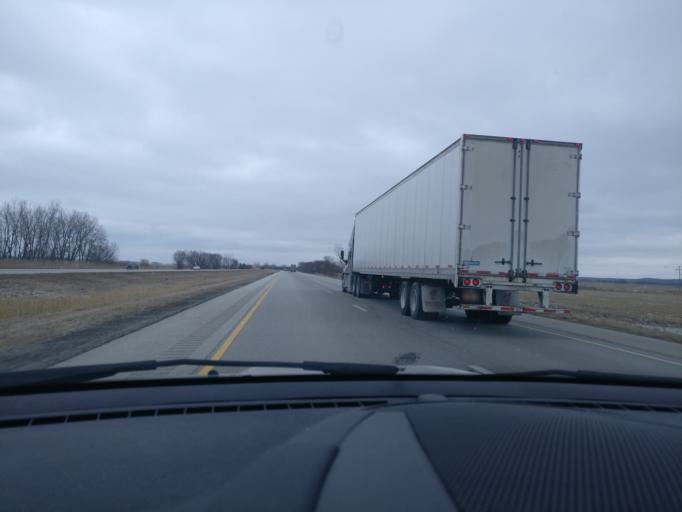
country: US
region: Illinois
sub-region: Henry County
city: Colona
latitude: 41.5367
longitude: -90.3007
